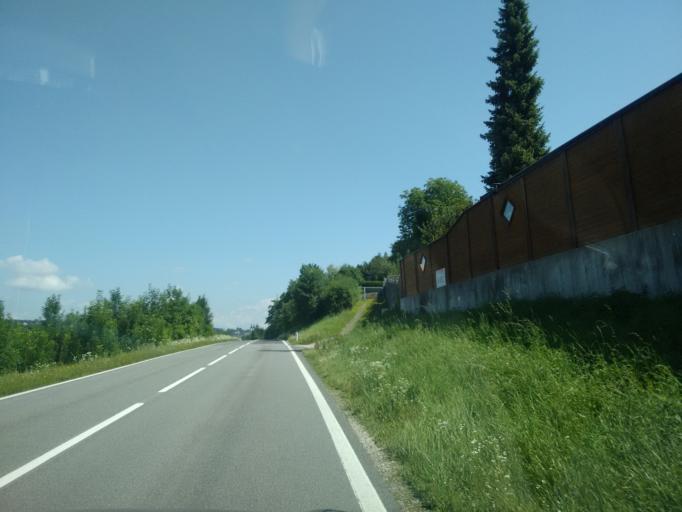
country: AT
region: Upper Austria
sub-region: Politischer Bezirk Kirchdorf an der Krems
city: Kremsmunster
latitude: 48.0349
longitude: 14.1232
